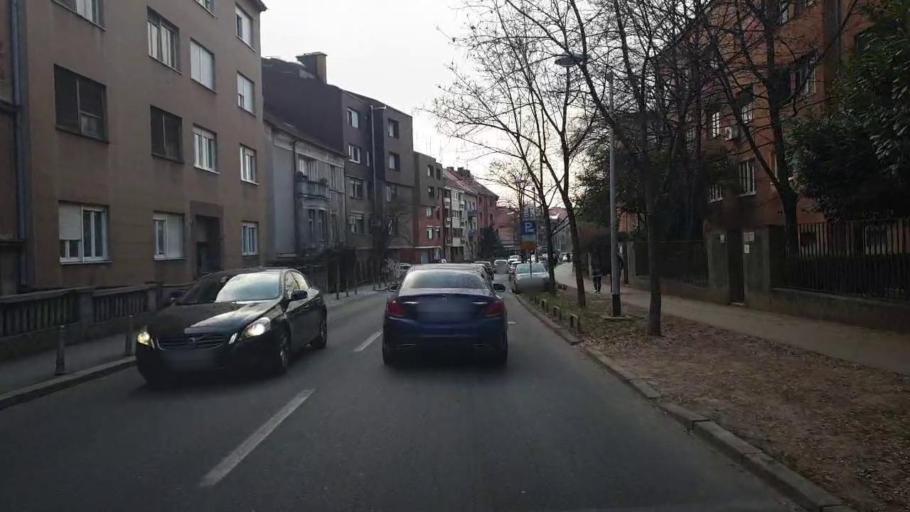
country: HR
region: Grad Zagreb
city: Zagreb
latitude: 45.8162
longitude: 15.9949
